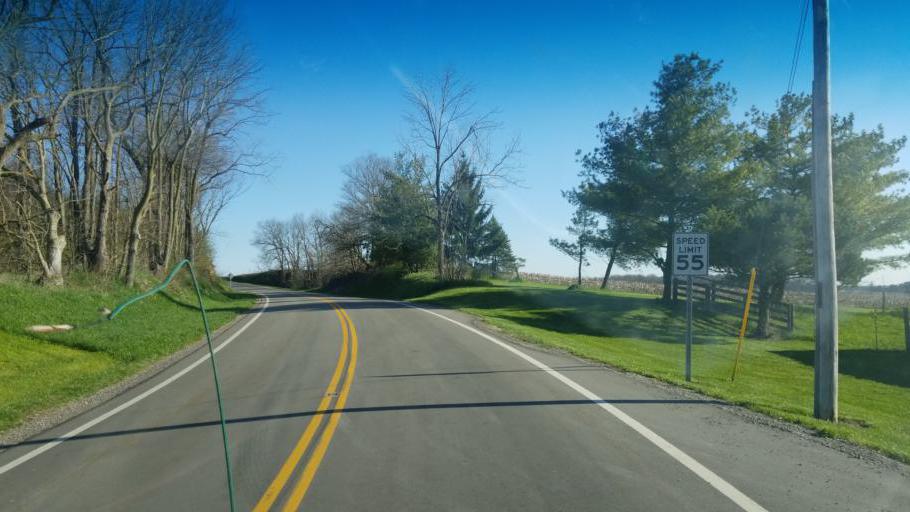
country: US
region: Ohio
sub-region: Logan County
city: Northwood
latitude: 40.4970
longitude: -83.6350
